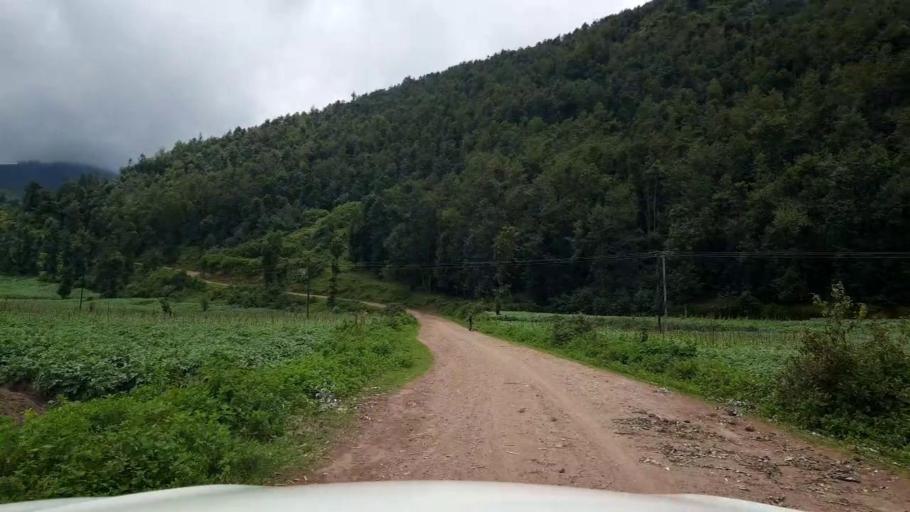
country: RW
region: Western Province
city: Gisenyi
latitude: -1.6476
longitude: 29.4108
